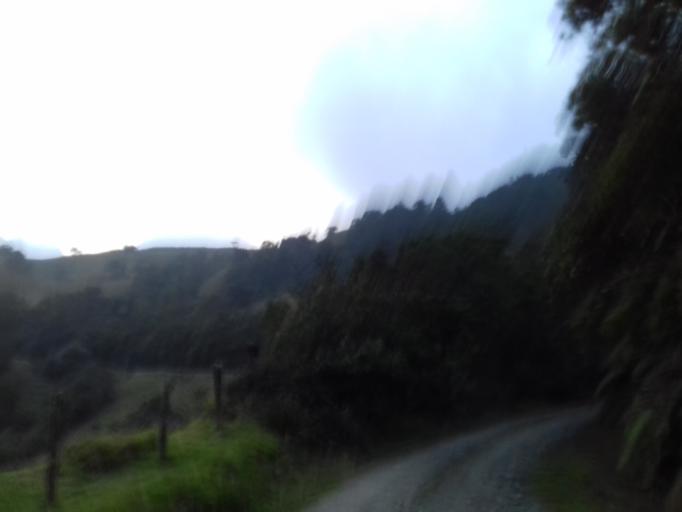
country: CO
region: Quindio
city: Salento
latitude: 4.5544
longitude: -75.5058
